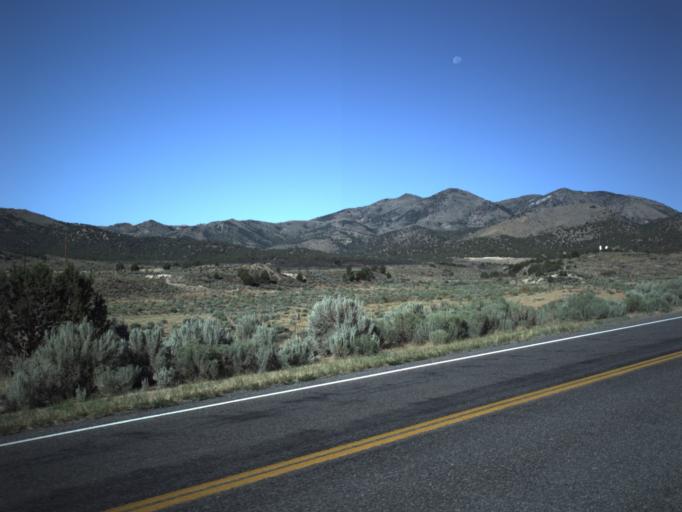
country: US
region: Utah
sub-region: Utah County
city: Genola
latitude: 39.9516
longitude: -112.0261
